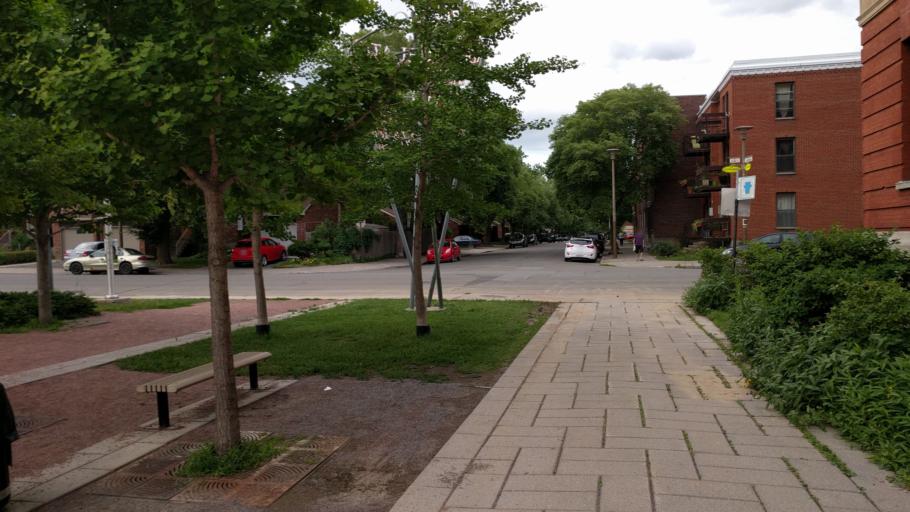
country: CA
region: Quebec
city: Westmount
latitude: 45.4837
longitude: -73.5753
